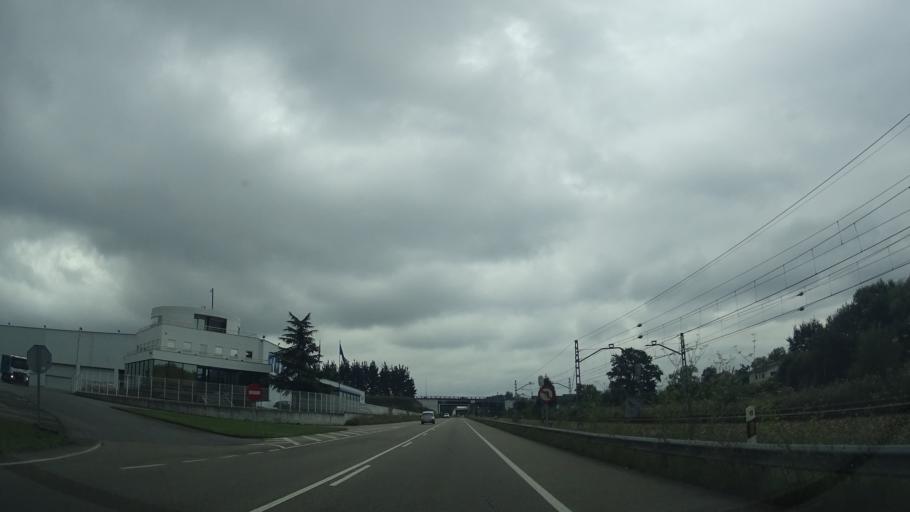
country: ES
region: Asturias
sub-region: Province of Asturias
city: Norena
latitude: 43.3815
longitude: -5.7417
